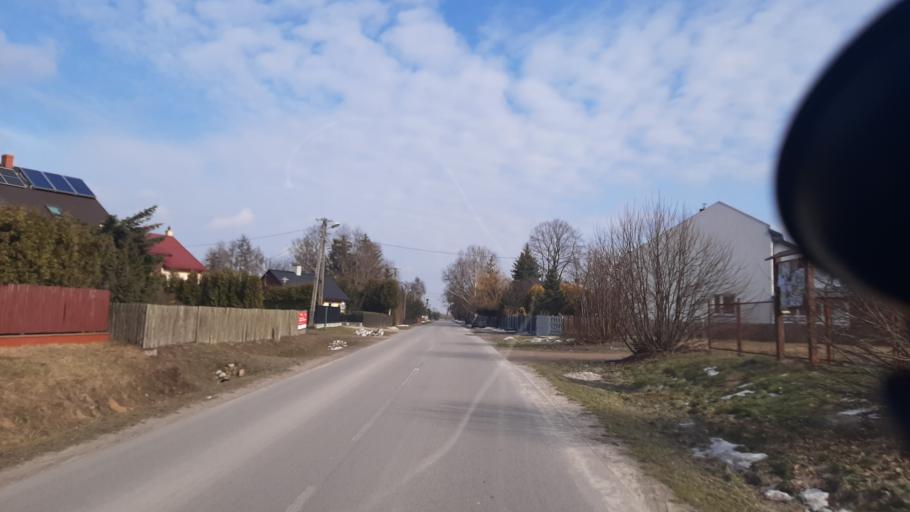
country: PL
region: Lublin Voivodeship
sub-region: Powiat lubartowski
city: Uscimow Stary
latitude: 51.4789
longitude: 22.9266
